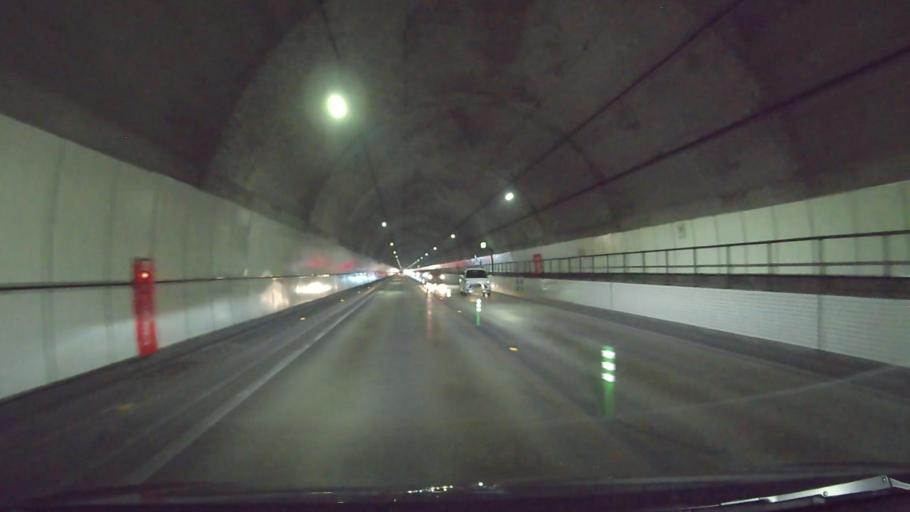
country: JP
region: Saitama
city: Yorii
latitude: 36.0919
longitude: 139.1411
